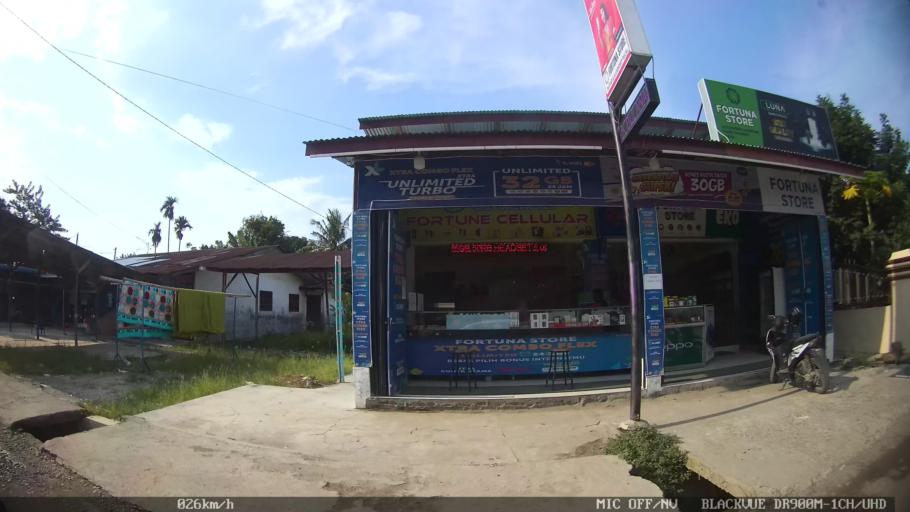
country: ID
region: North Sumatra
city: Medan
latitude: 3.6054
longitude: 98.7411
